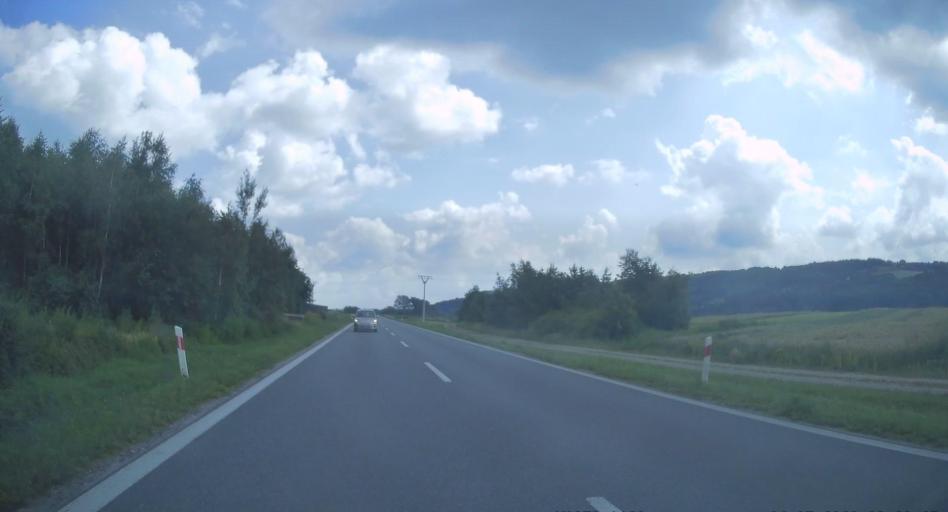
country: PL
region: Lesser Poland Voivodeship
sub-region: Powiat tarnowski
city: Wielka Wies
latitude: 49.9284
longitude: 20.8388
